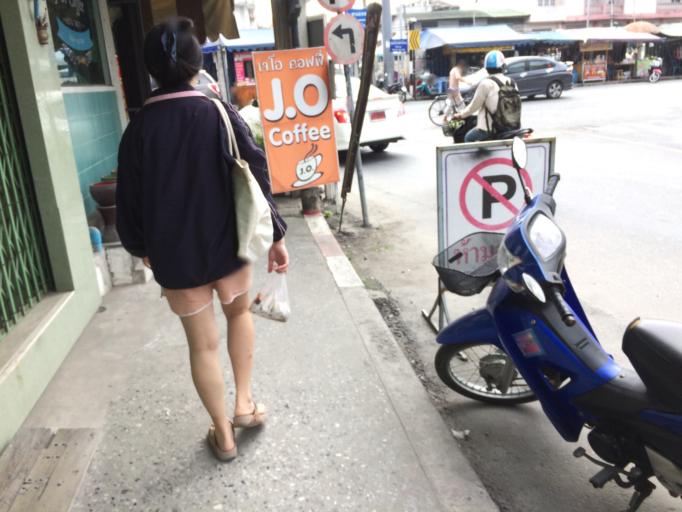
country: TH
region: Chon Buri
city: Ban Bueng
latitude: 13.3113
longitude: 101.1141
